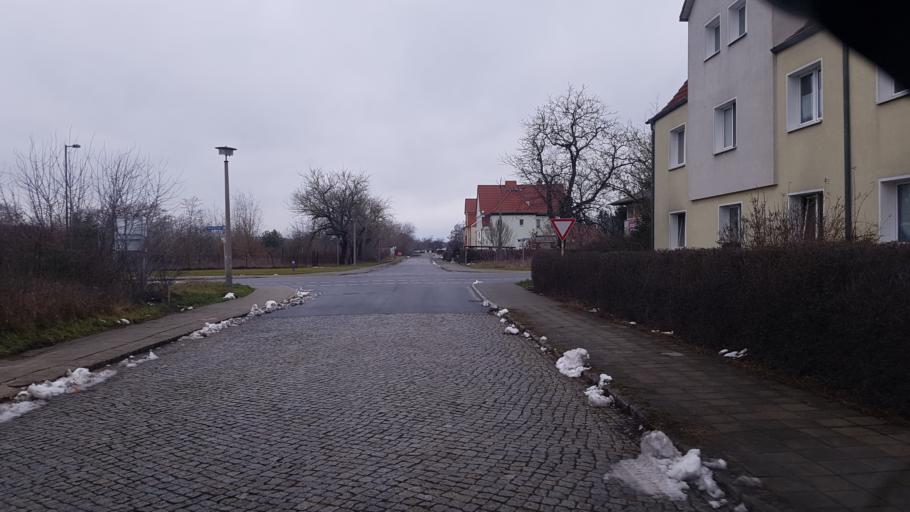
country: DE
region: Brandenburg
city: Eisenhuettenstadt
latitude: 52.1507
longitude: 14.6544
